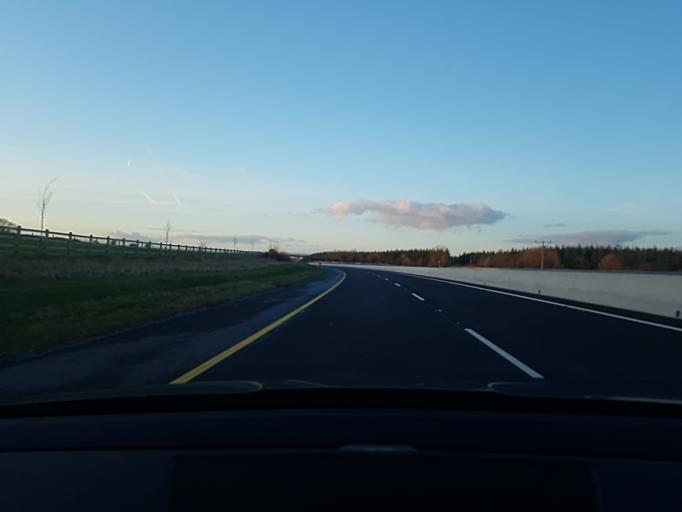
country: IE
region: Connaught
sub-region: County Galway
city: Tuam
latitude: 53.4884
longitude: -8.8655
